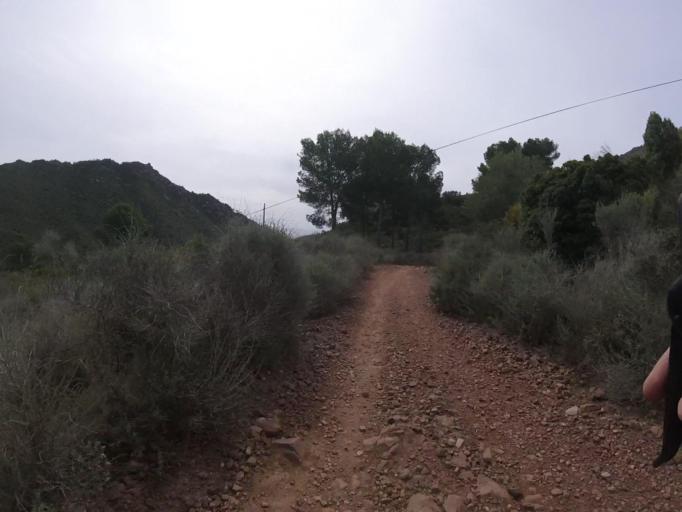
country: ES
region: Valencia
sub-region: Provincia de Castello
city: Benicassim
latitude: 40.0708
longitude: 0.0363
